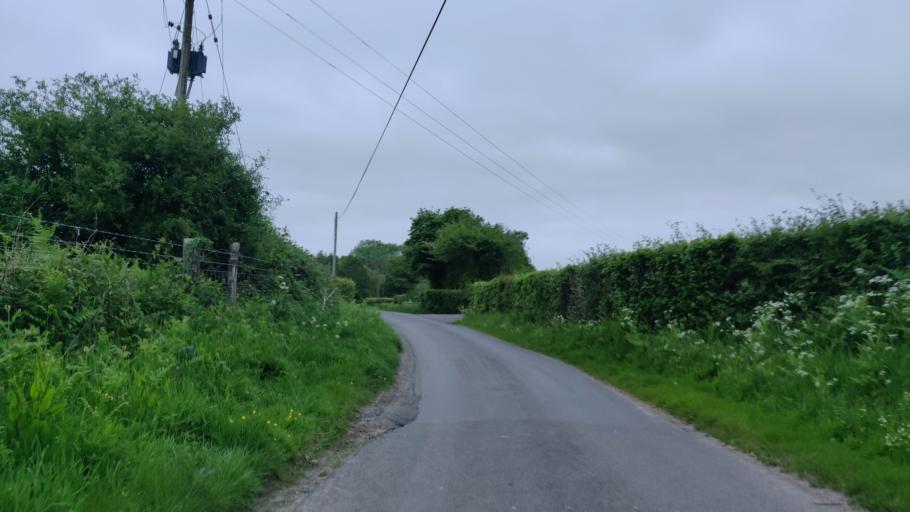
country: GB
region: England
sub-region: West Sussex
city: Southwater
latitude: 51.0321
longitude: -0.3335
